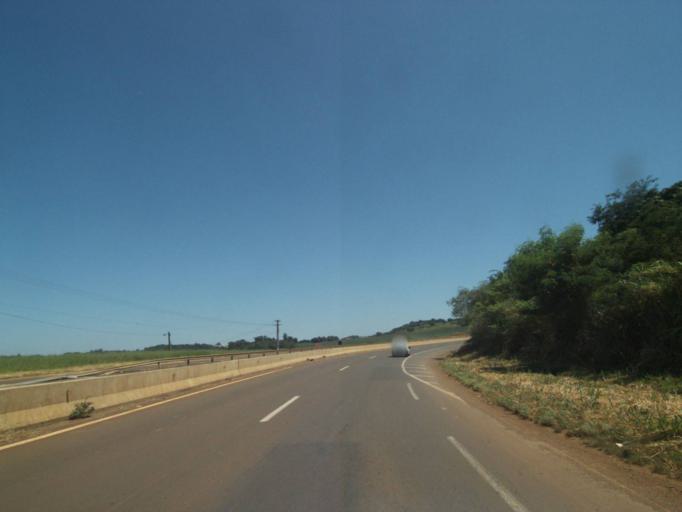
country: BR
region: Parana
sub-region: Londrina
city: Londrina
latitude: -23.3867
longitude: -51.1354
